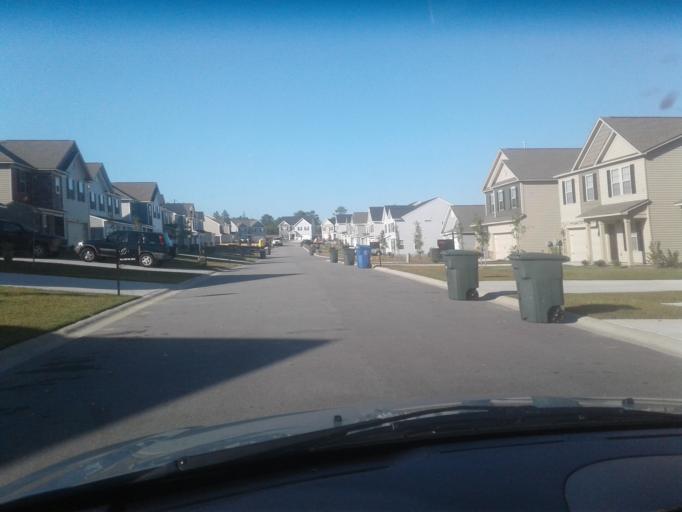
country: US
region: South Carolina
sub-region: Richland County
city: Woodfield
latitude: 34.0774
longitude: -80.8909
